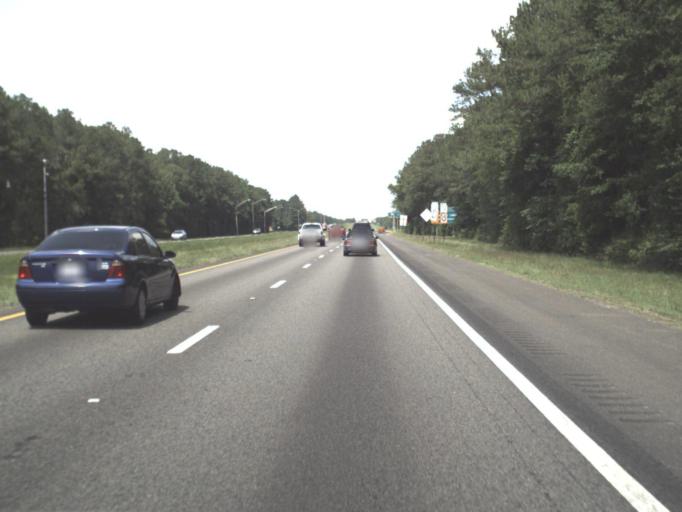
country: US
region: Florida
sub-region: Nassau County
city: Nassau Village-Ratliff
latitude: 30.4302
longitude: -81.7294
